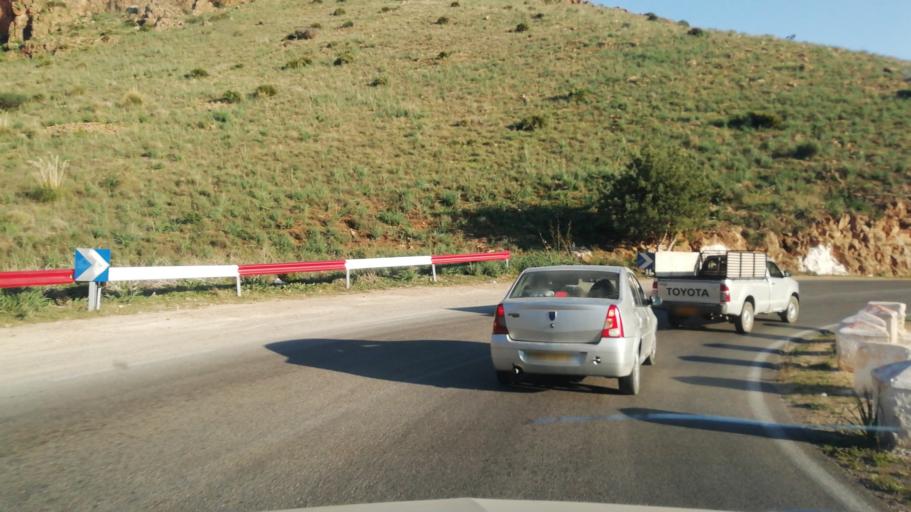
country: DZ
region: Tlemcen
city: Beni Mester
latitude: 34.8429
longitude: -1.4634
